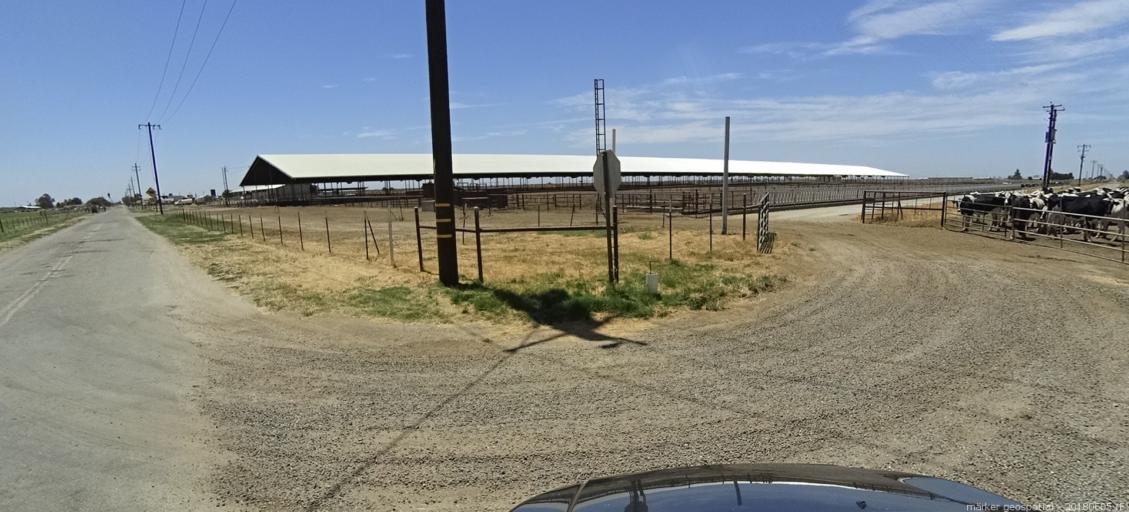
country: US
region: California
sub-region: Madera County
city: Chowchilla
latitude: 37.0982
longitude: -120.3290
